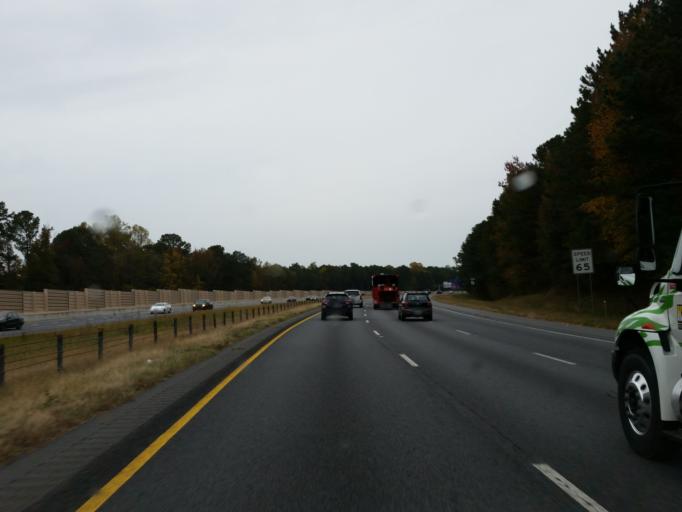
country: US
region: Georgia
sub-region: Cherokee County
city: Woodstock
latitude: 34.1092
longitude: -84.5337
